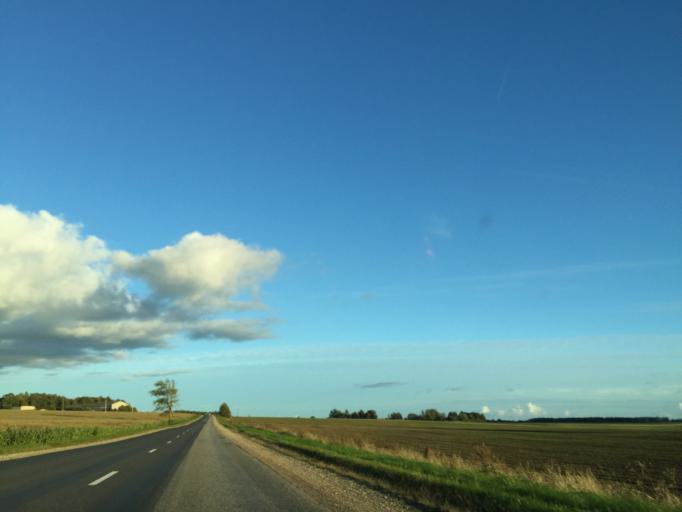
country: LV
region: Saldus Rajons
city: Saldus
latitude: 56.7103
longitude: 22.4156
